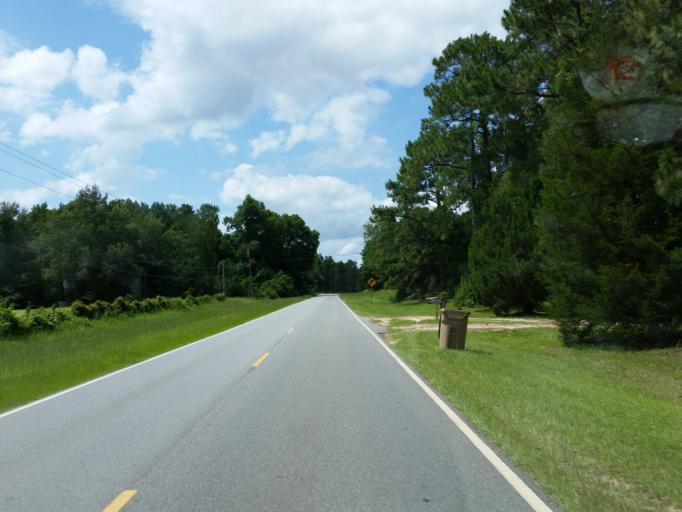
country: US
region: Georgia
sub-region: Tift County
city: Unionville
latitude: 31.3976
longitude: -83.5170
